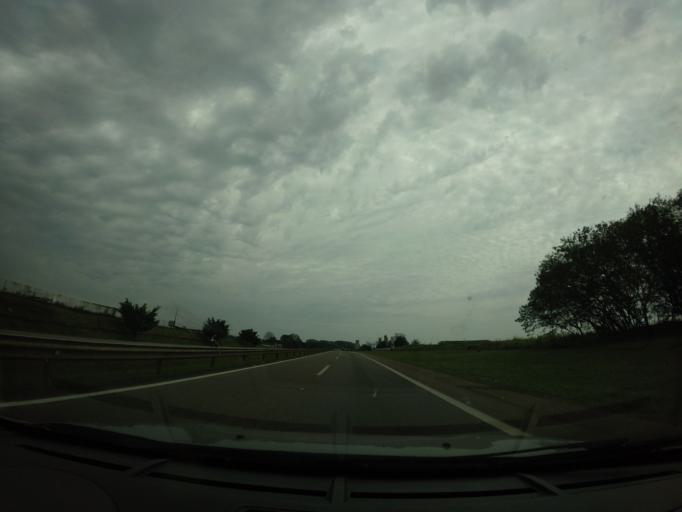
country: BR
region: Sao Paulo
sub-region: Piracicaba
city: Piracicaba
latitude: -22.7298
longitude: -47.6032
